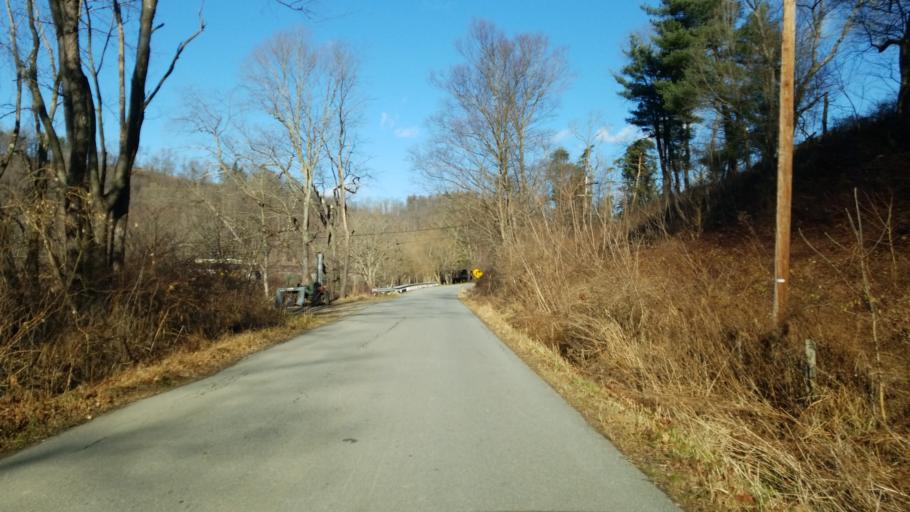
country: US
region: Pennsylvania
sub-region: Clearfield County
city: Curwensville
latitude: 40.9787
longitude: -78.4935
